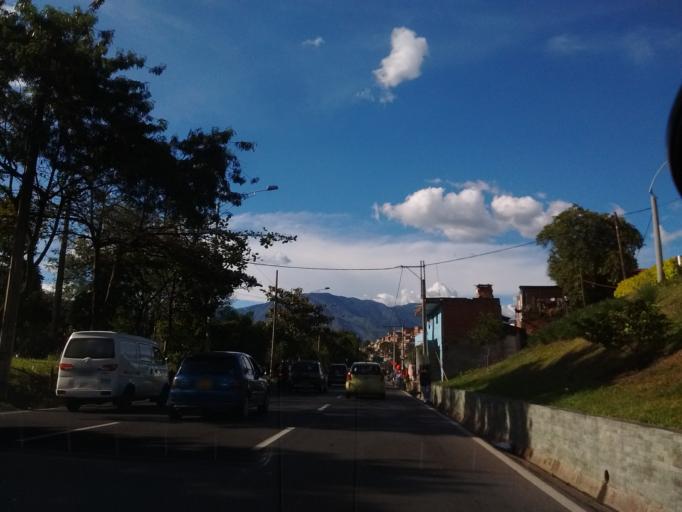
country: CO
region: Antioquia
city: Medellin
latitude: 6.2778
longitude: -75.5687
